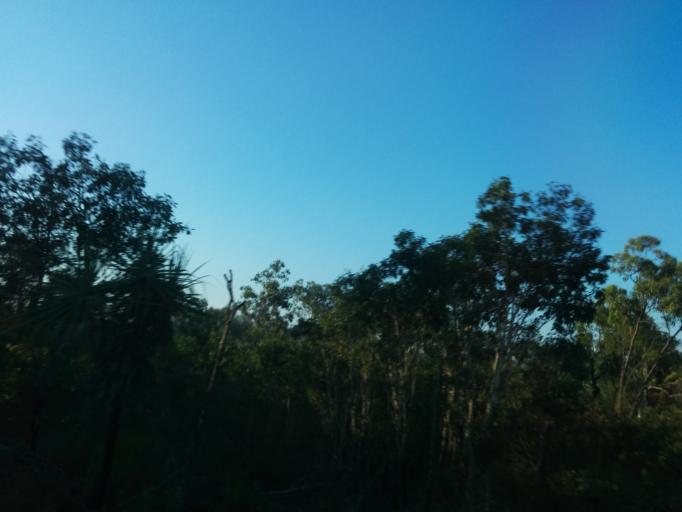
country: AU
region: Northern Territory
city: Alyangula
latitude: -13.8725
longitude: 136.7847
